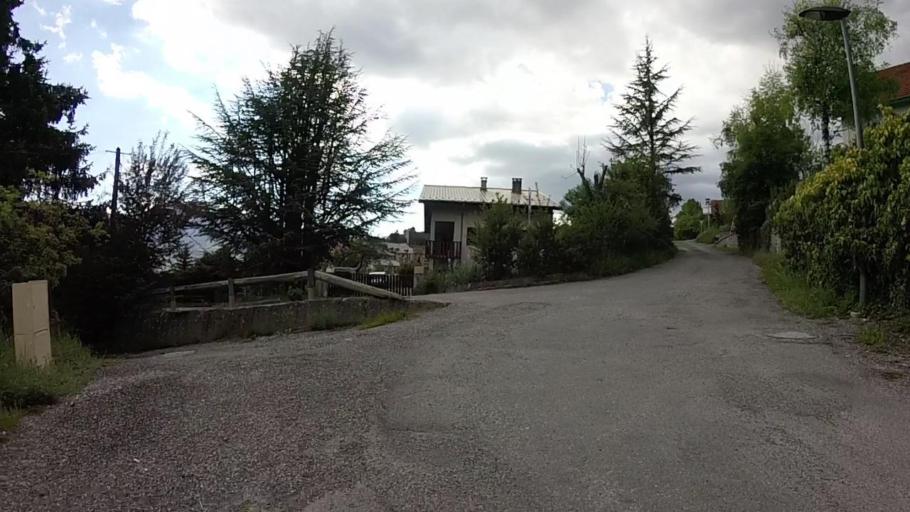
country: FR
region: Provence-Alpes-Cote d'Azur
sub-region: Departement des Alpes-de-Haute-Provence
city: Seyne-les-Alpes
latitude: 44.3507
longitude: 6.3599
